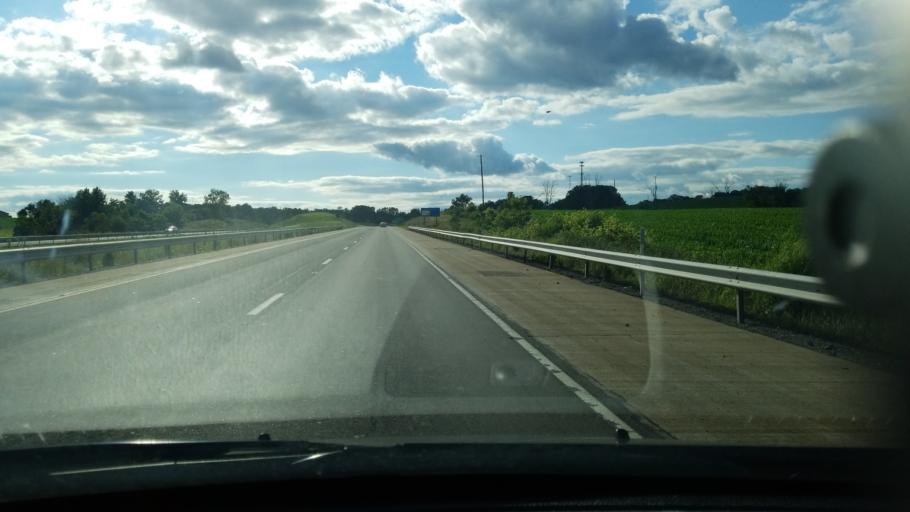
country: US
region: Pennsylvania
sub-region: Northumberland County
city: Milton
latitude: 41.0102
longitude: -76.7759
